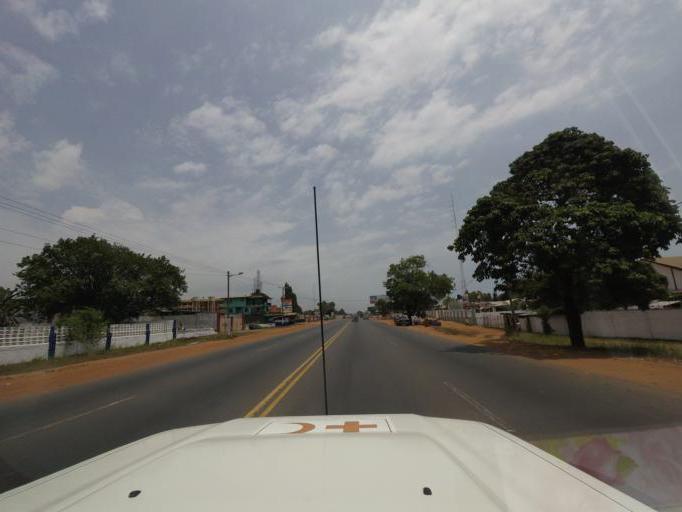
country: LR
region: Montserrado
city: Monrovia
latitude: 6.2779
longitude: -10.7585
